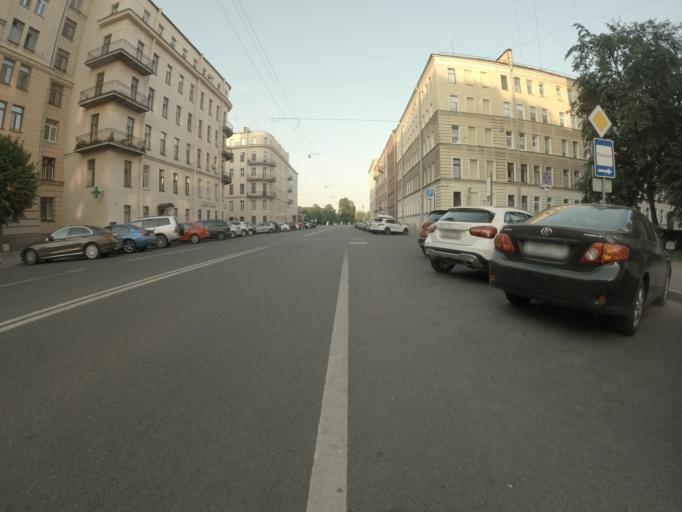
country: RU
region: St.-Petersburg
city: Centralniy
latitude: 59.9468
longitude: 30.3871
